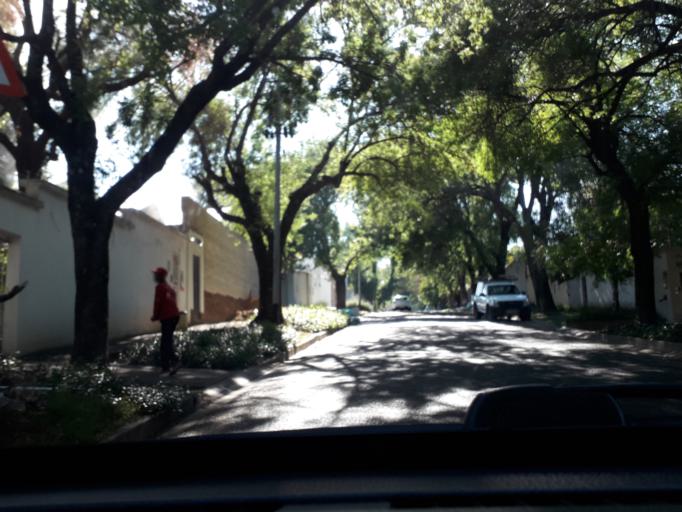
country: ZA
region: Gauteng
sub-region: City of Johannesburg Metropolitan Municipality
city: Johannesburg
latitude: -26.1442
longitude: 28.0187
